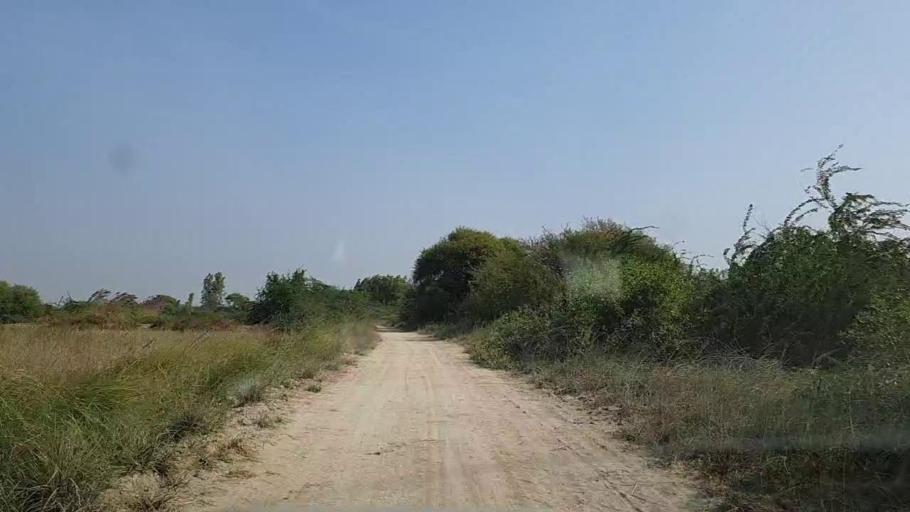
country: PK
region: Sindh
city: Mirpur Sakro
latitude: 24.5526
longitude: 67.5618
